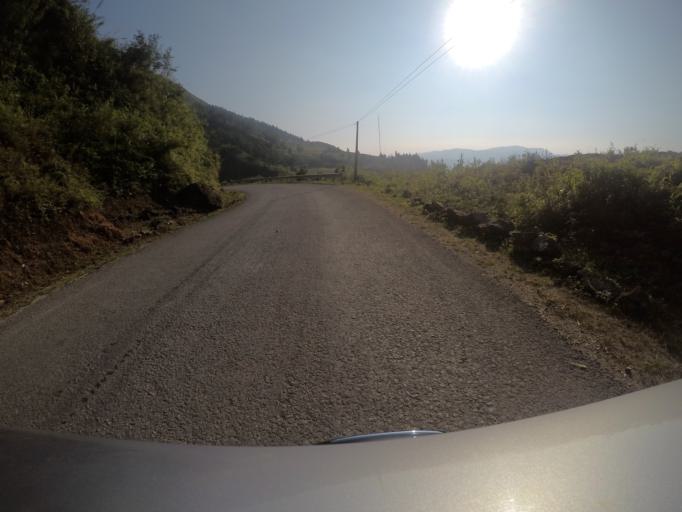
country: VN
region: Lai Chau
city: Than Uyen
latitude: 22.0329
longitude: 103.9395
